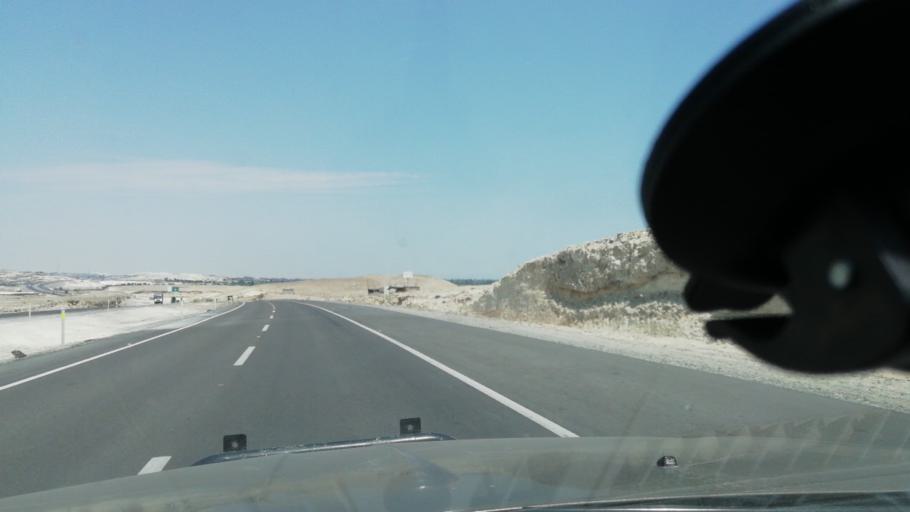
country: PE
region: Ica
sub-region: Provincia de Pisco
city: San Clemente
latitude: -13.6611
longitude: -76.1737
